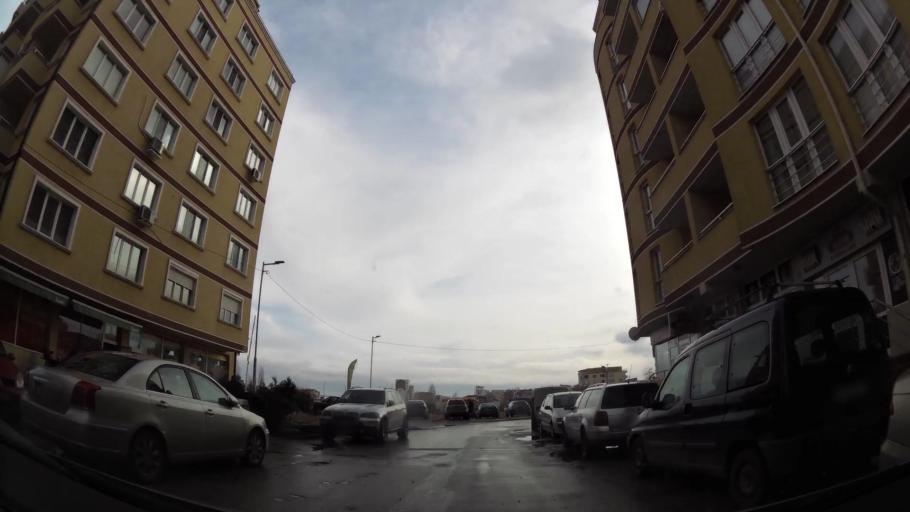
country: BG
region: Sofiya
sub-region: Obshtina Bozhurishte
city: Bozhurishte
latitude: 42.7199
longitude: 23.2521
